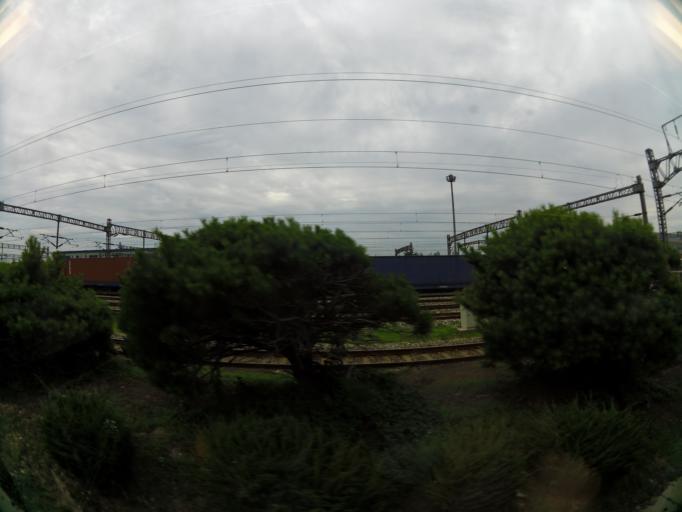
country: KR
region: Gyeonggi-do
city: Suwon-si
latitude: 37.3190
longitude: 126.9481
